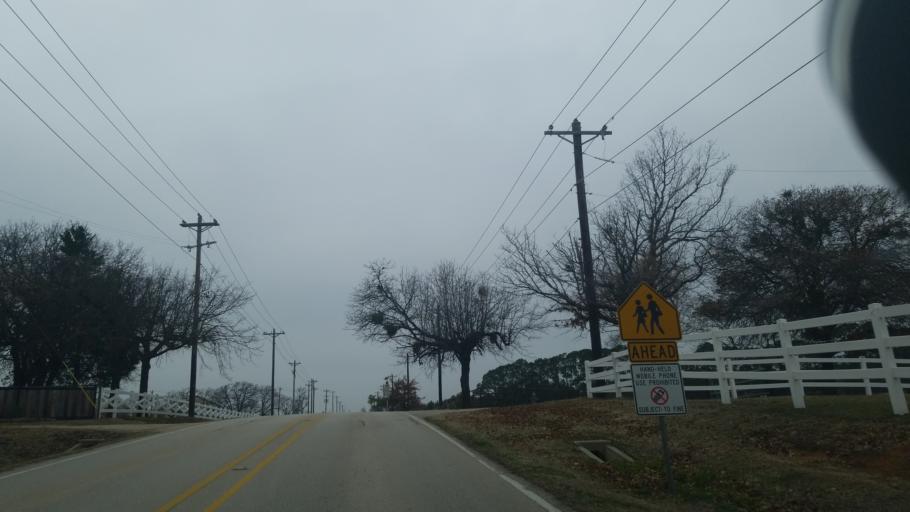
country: US
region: Texas
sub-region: Denton County
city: Copper Canyon
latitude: 33.1178
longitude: -97.1197
